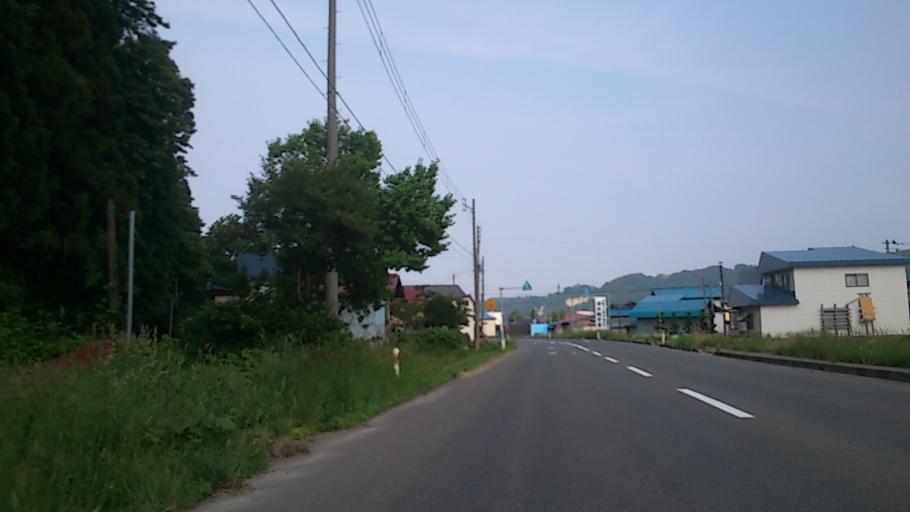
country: JP
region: Aomori
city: Hirosaki
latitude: 40.5906
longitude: 140.3311
